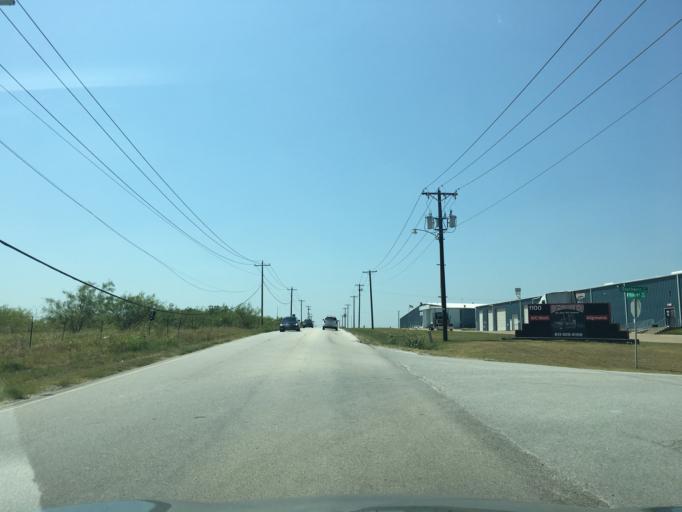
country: US
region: Texas
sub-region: Tarrant County
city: Edgecliff Village
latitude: 32.6141
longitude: -97.3335
